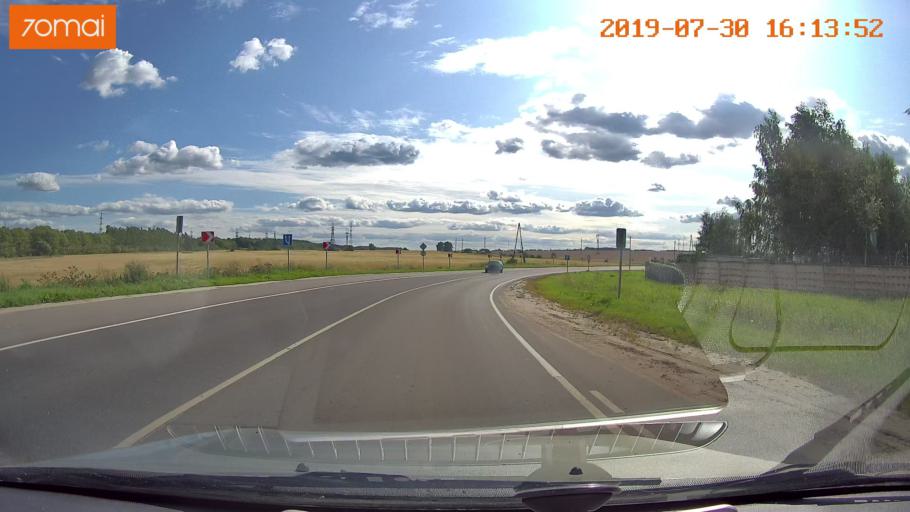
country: RU
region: Moskovskaya
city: Voskresensk
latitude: 55.2883
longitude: 38.6888
